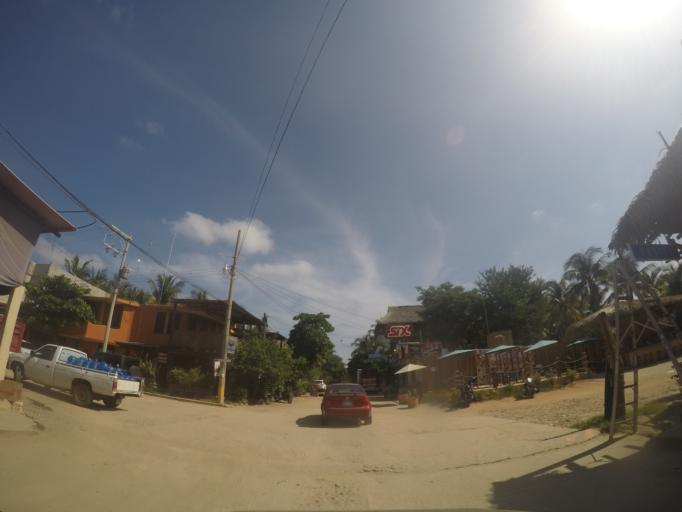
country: MX
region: Oaxaca
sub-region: Santa Maria Colotepec
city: Brisas de Zicatela
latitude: 15.8340
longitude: -97.0447
